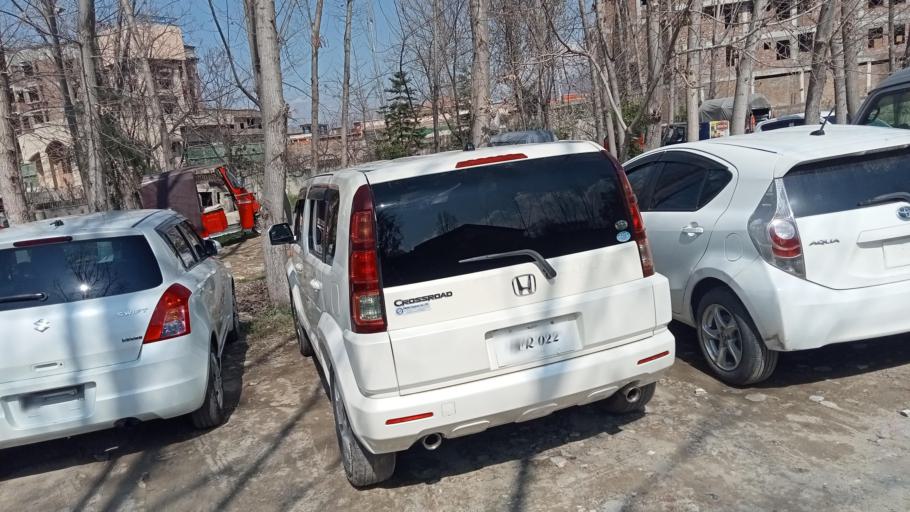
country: PK
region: Khyber Pakhtunkhwa
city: Saidu Sharif
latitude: 34.7470
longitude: 72.3542
